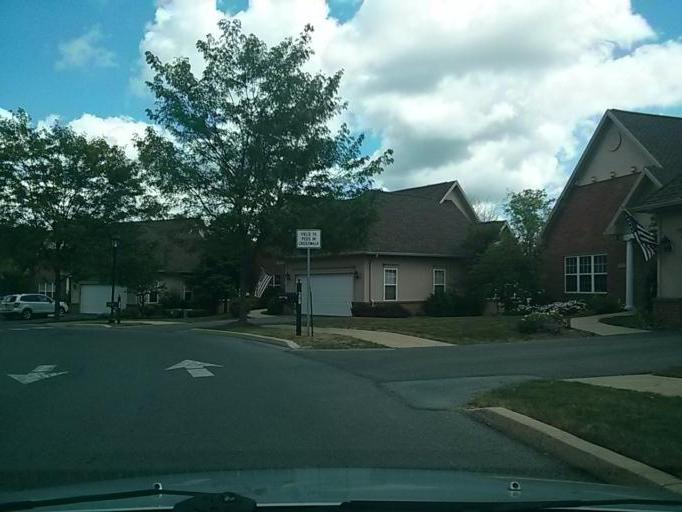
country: US
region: Pennsylvania
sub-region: Centre County
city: State College
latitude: 40.8243
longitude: -77.8719
